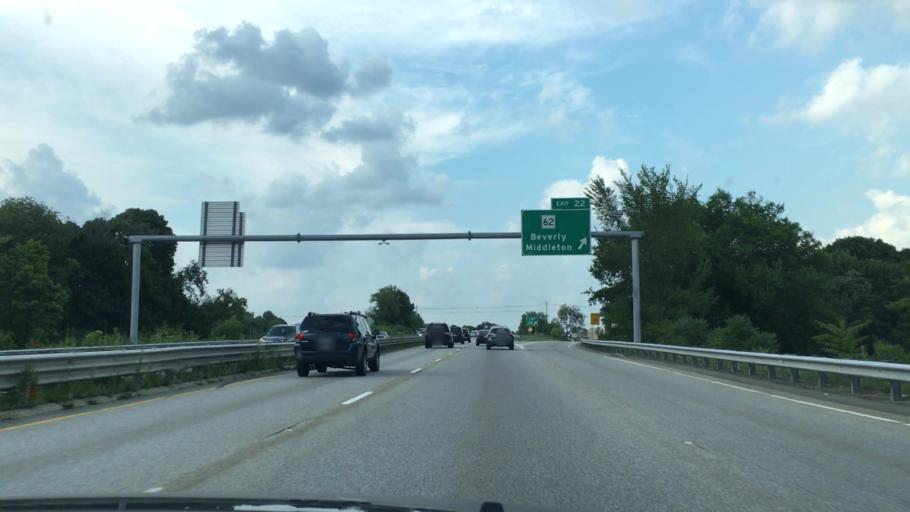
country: US
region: Massachusetts
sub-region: Essex County
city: Danvers
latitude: 42.5630
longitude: -70.9245
